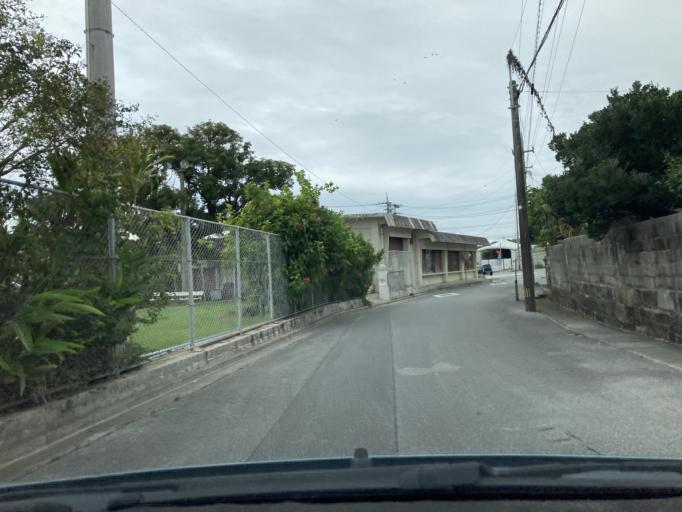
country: JP
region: Okinawa
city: Tomigusuku
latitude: 26.1735
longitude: 127.7139
